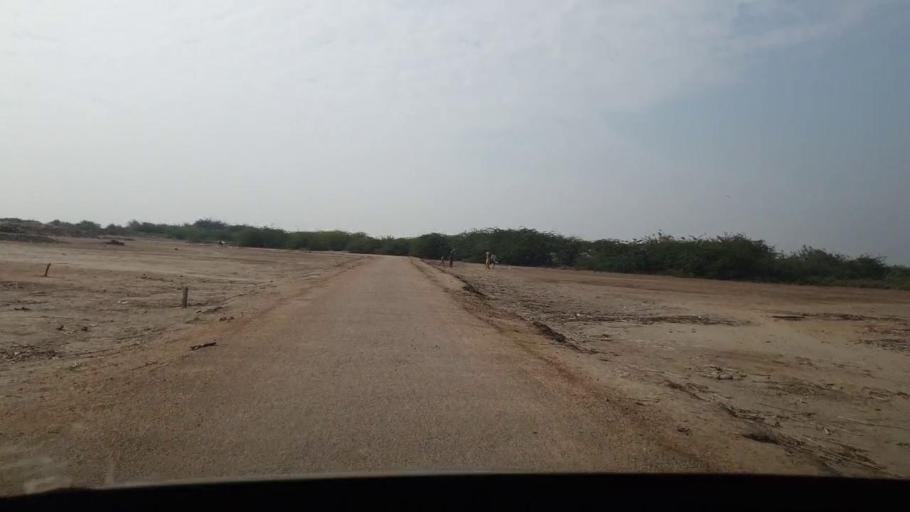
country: PK
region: Sindh
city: Chuhar Jamali
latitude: 24.2359
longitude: 67.9840
